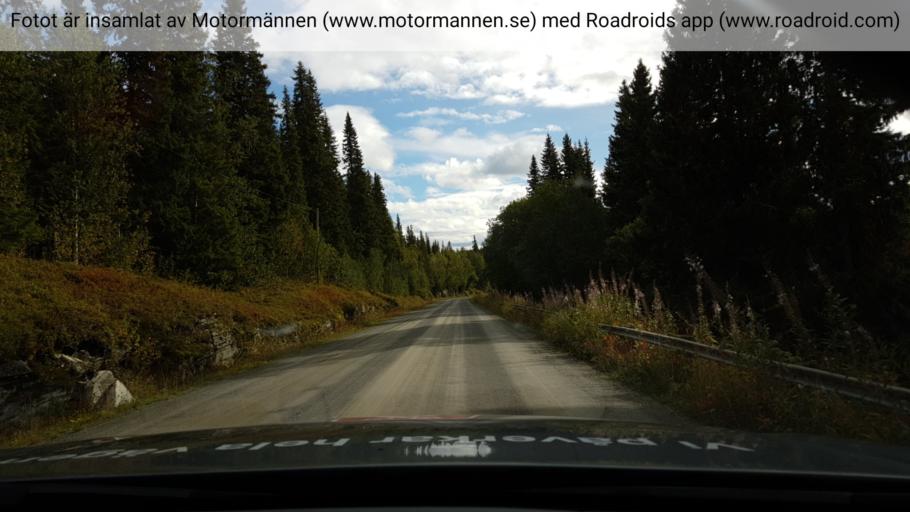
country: SE
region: Jaemtland
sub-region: Are Kommun
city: Are
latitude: 63.6908
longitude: 12.8055
